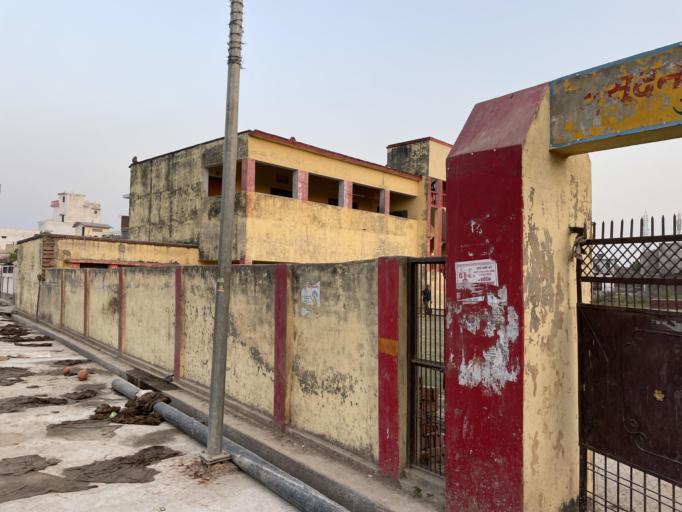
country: IN
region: Uttar Pradesh
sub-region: Faizabad
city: Ayodhya
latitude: 26.8038
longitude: 82.2029
